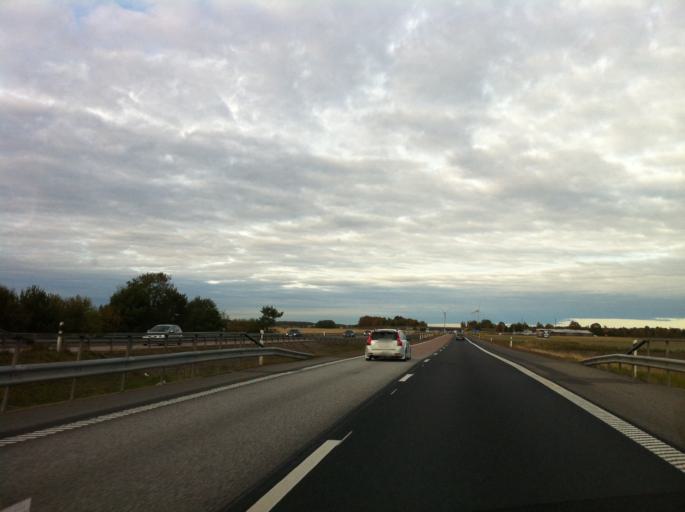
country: SE
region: OErebro
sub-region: Kumla Kommun
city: Kumla
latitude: 59.1346
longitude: 15.0791
